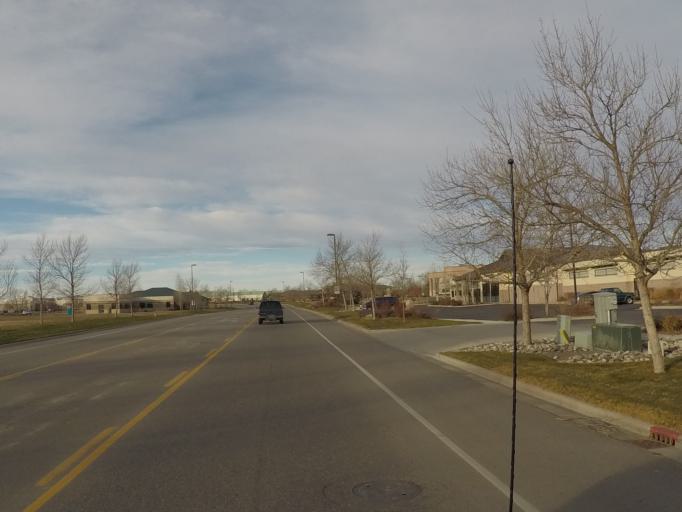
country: US
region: Montana
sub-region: Yellowstone County
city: Billings
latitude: 45.7443
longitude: -108.6005
